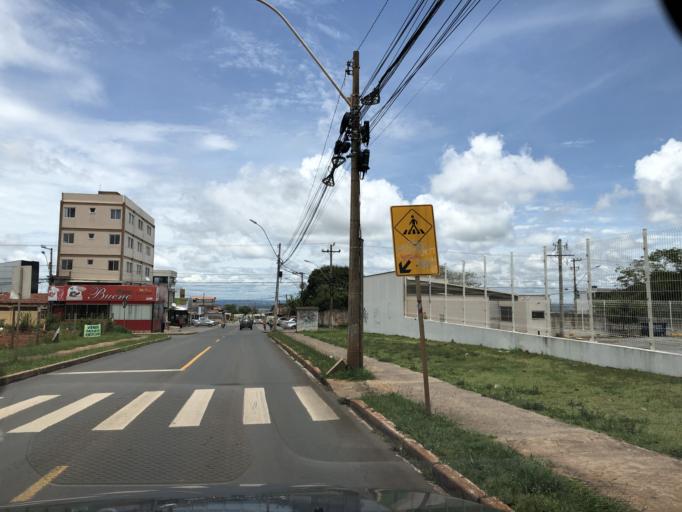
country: BR
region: Federal District
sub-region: Brasilia
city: Brasilia
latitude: -15.8352
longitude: -48.1123
